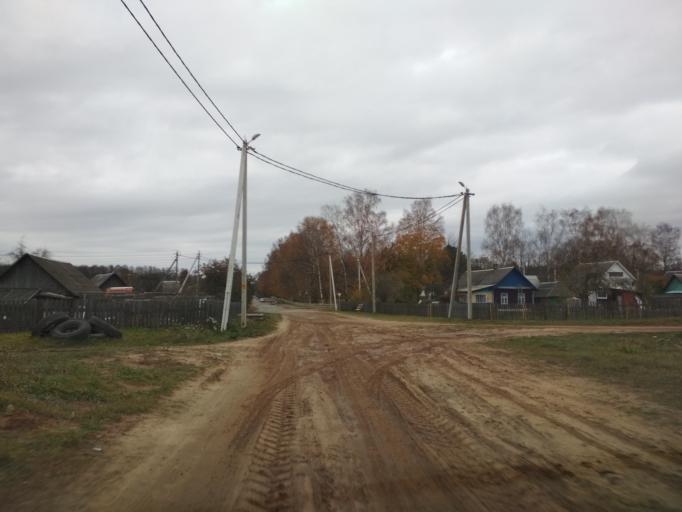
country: BY
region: Minsk
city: Blon'
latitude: 53.5213
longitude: 28.1773
